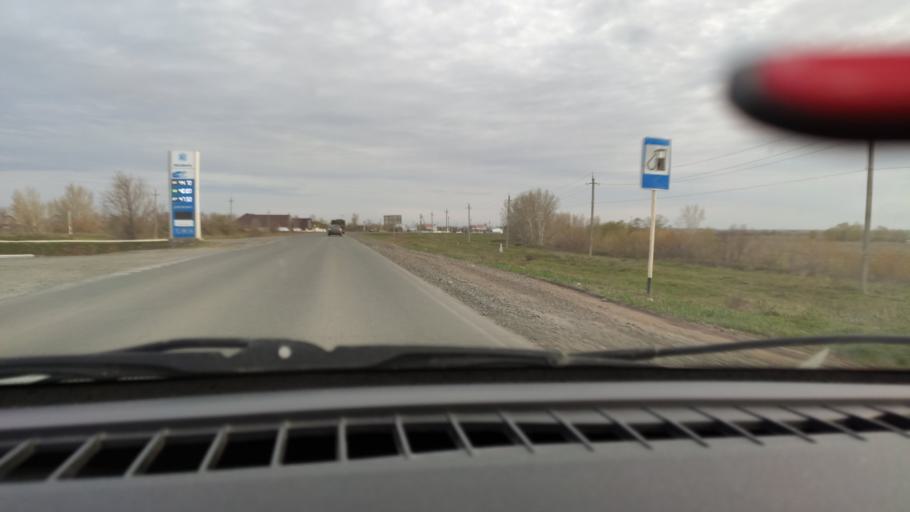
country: RU
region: Orenburg
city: Tatarskaya Kargala
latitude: 51.9055
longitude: 55.1712
